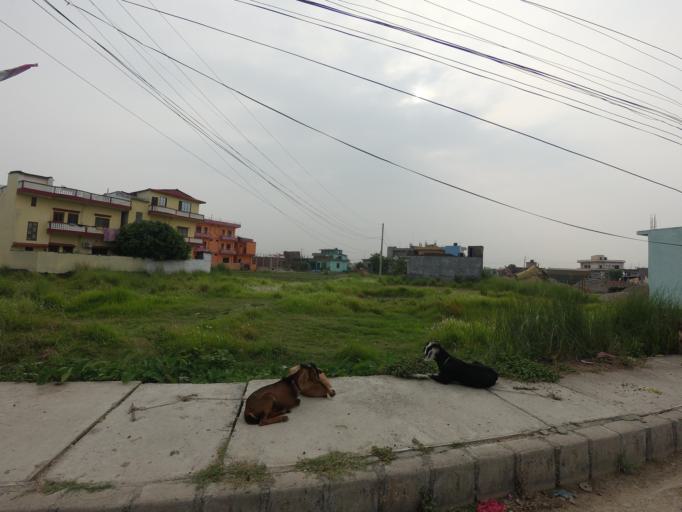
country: NP
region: Western Region
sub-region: Lumbini Zone
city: Bhairahawa
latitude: 27.4914
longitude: 83.4517
